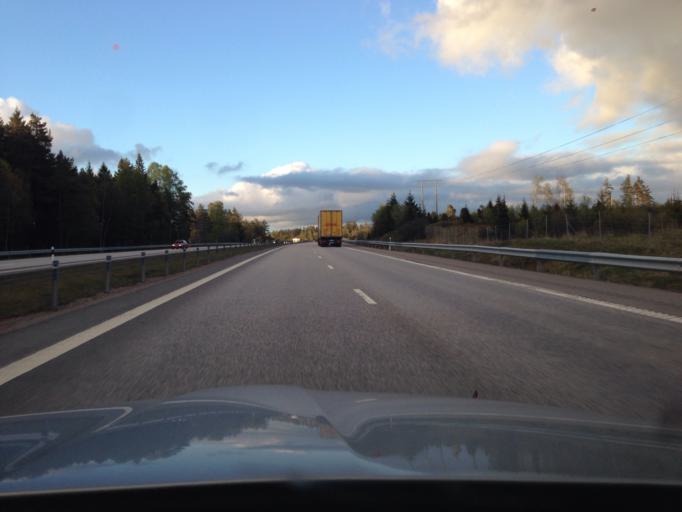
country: SE
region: Soedermanland
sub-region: Oxelosunds Kommun
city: Oxelosund
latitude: 58.8265
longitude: 17.1569
